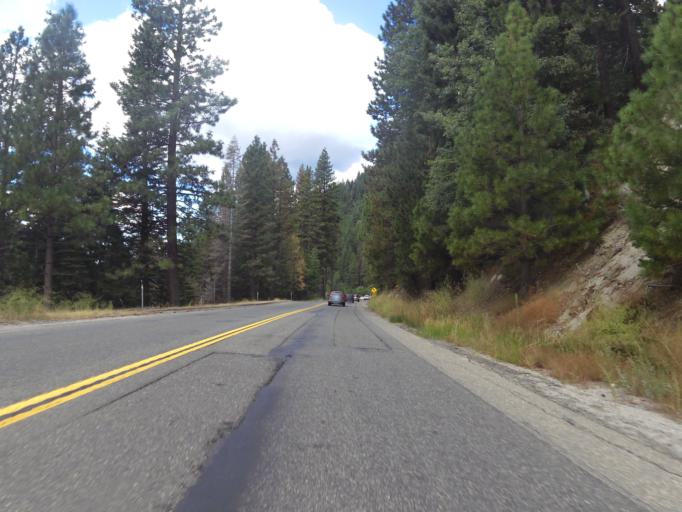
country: US
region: California
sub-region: El Dorado County
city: South Lake Tahoe
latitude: 38.7835
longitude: -120.2317
